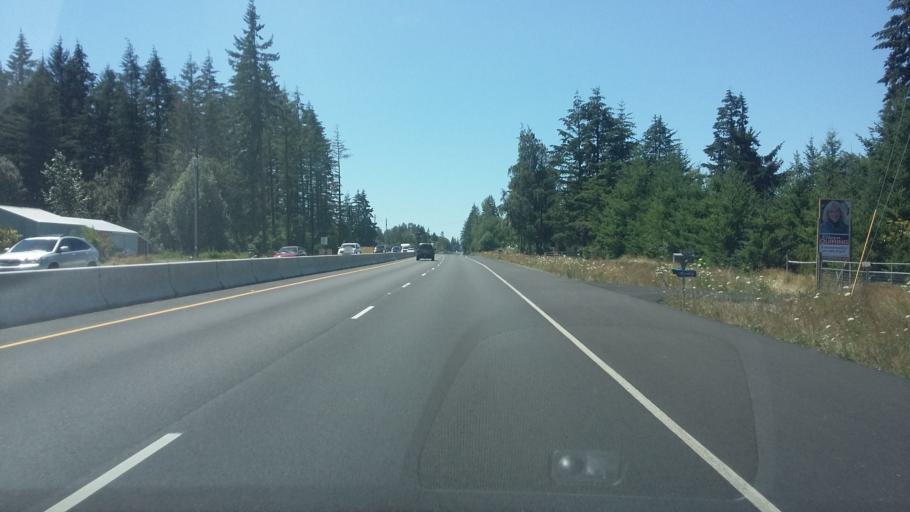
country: US
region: Washington
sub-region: Clark County
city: Dollar Corner
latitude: 45.7799
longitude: -122.6223
